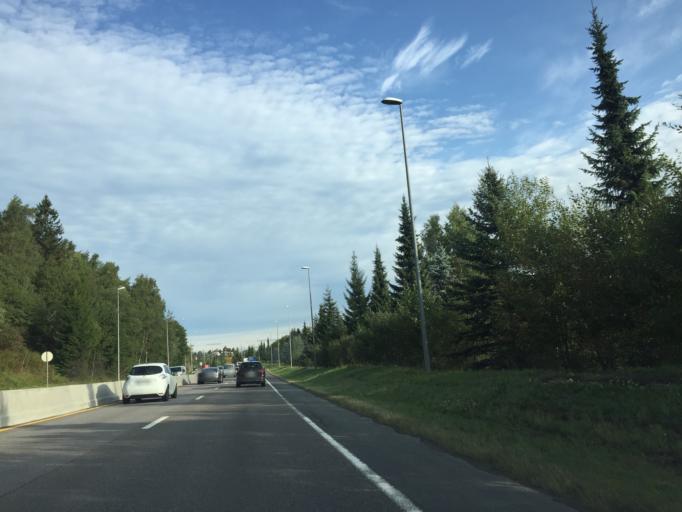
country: NO
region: Akershus
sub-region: Oppegard
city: Kolbotn
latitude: 59.8731
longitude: 10.8252
